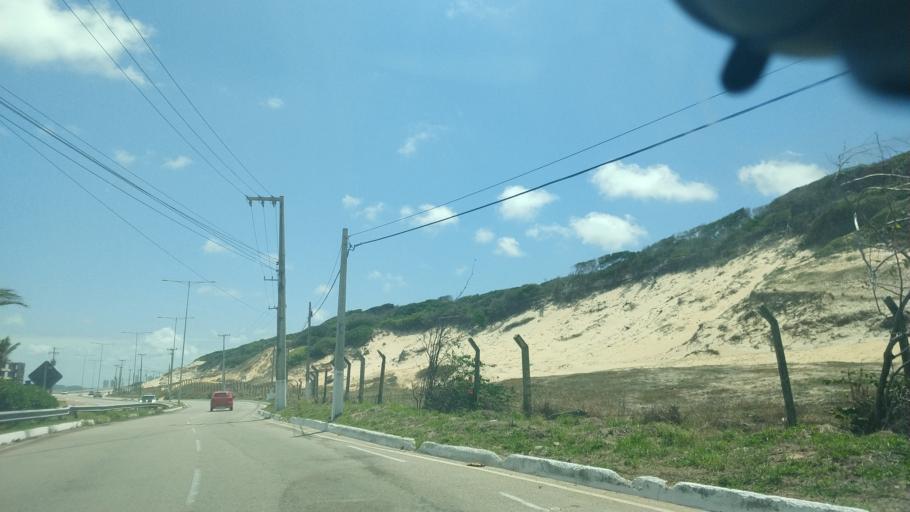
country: BR
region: Rio Grande do Norte
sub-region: Natal
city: Natal
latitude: -5.8316
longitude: -35.1832
